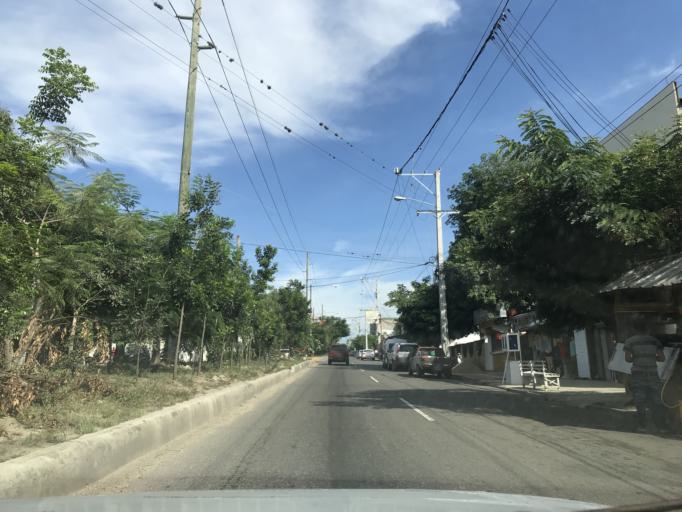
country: DO
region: Santiago
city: Santiago de los Caballeros
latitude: 19.4484
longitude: -70.7431
